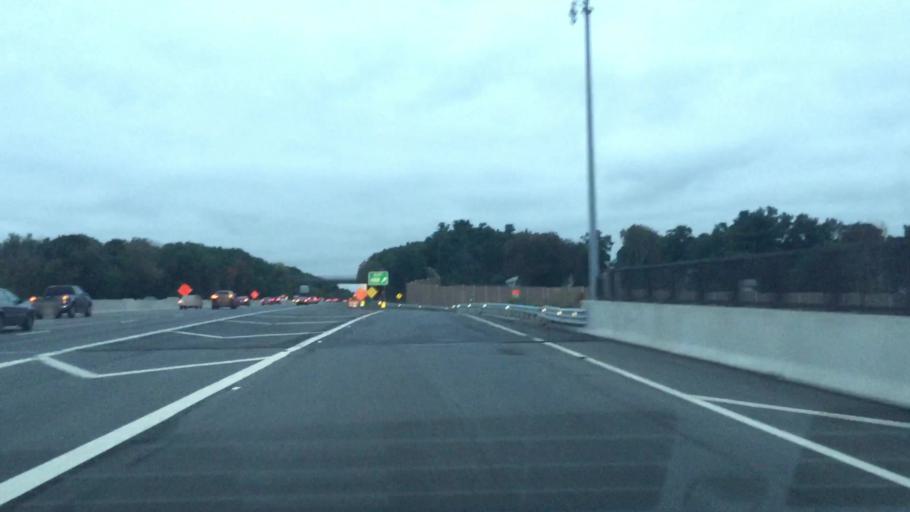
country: US
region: Massachusetts
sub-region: Essex County
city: Methuen
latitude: 42.7052
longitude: -71.2102
